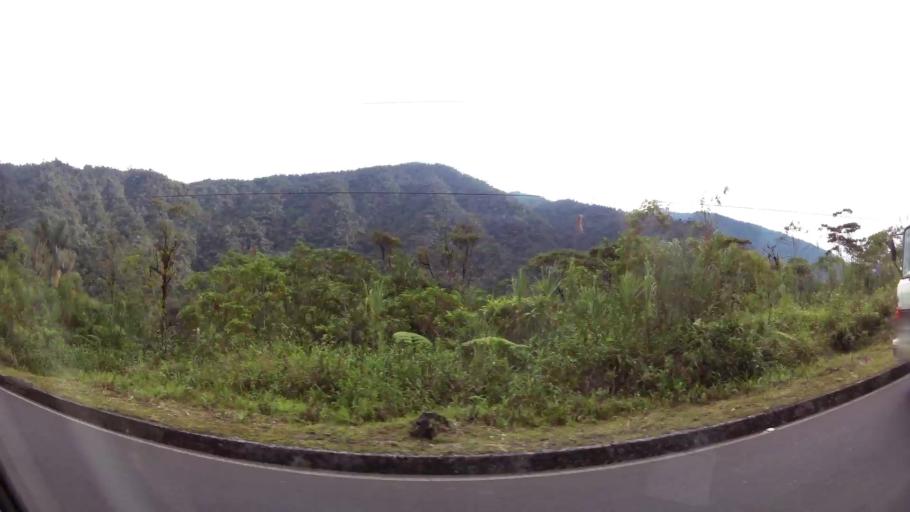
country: EC
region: Pastaza
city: Puyo
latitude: -1.4503
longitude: -78.1551
